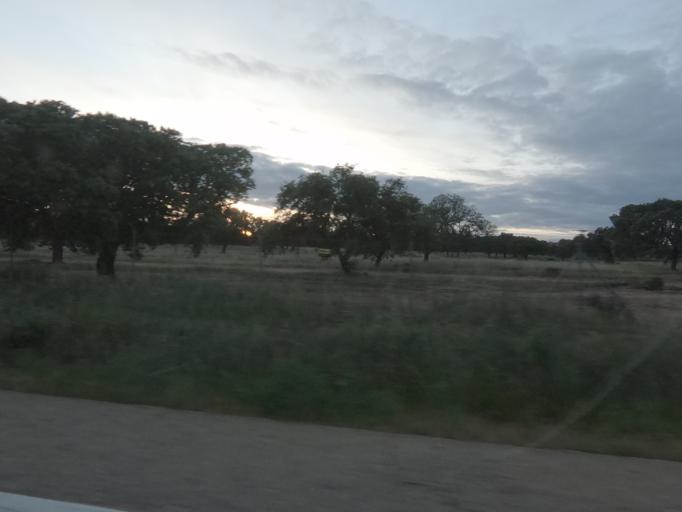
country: ES
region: Extremadura
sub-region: Provincia de Badajoz
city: Villar del Rey
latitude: 38.9996
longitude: -6.8666
